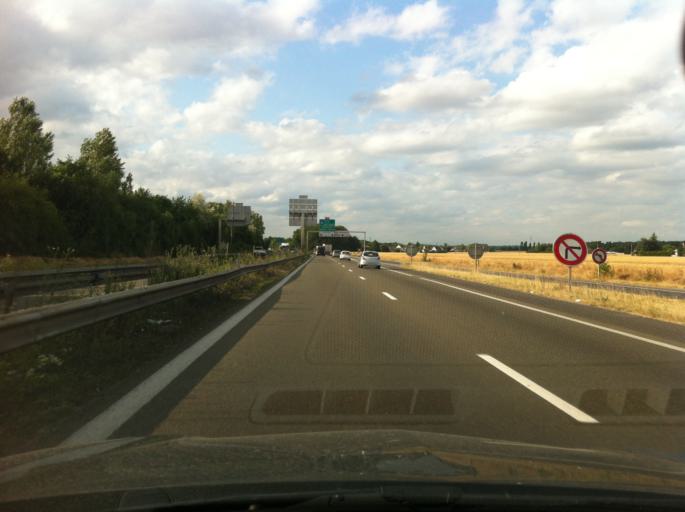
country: FR
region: Ile-de-France
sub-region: Departement de Seine-et-Marne
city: Servon
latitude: 48.7103
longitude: 2.5994
